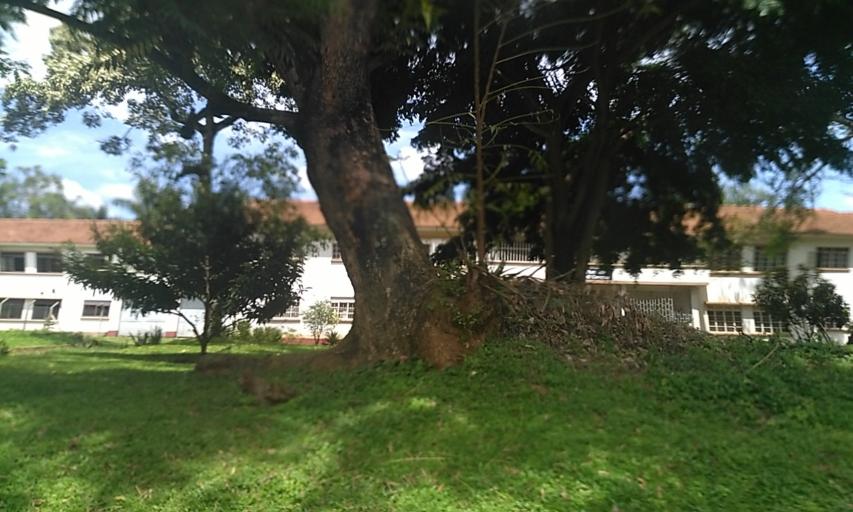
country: UG
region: Central Region
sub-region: Kampala District
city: Kampala
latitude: 0.3212
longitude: 32.5951
